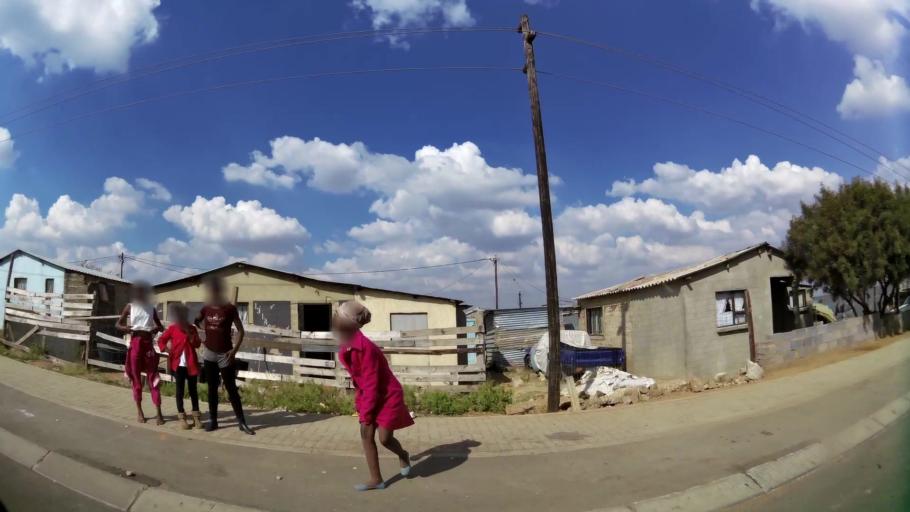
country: ZA
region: Gauteng
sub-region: City of Johannesburg Metropolitan Municipality
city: Roodepoort
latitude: -26.1930
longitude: 27.8756
